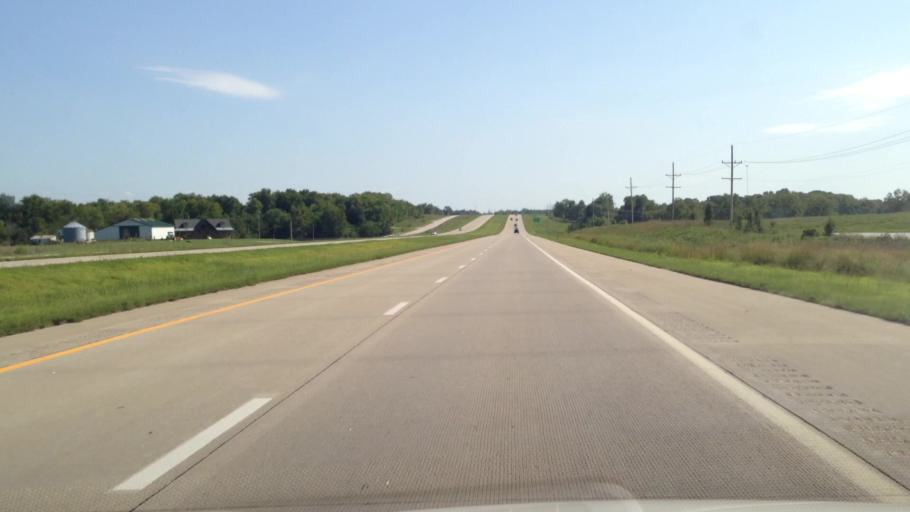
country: US
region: Kansas
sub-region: Linn County
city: Pleasanton
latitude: 38.2068
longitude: -94.7056
